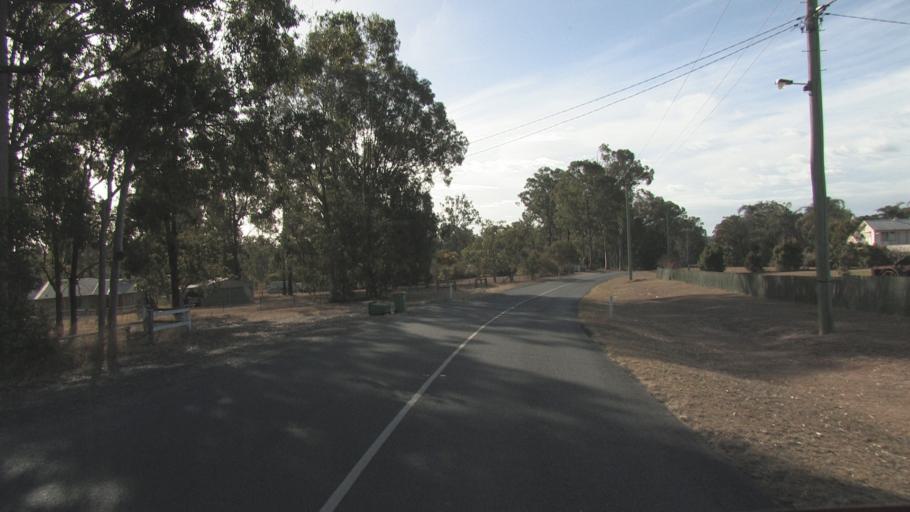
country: AU
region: Queensland
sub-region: Logan
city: Cedar Vale
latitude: -27.8728
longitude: 153.0106
